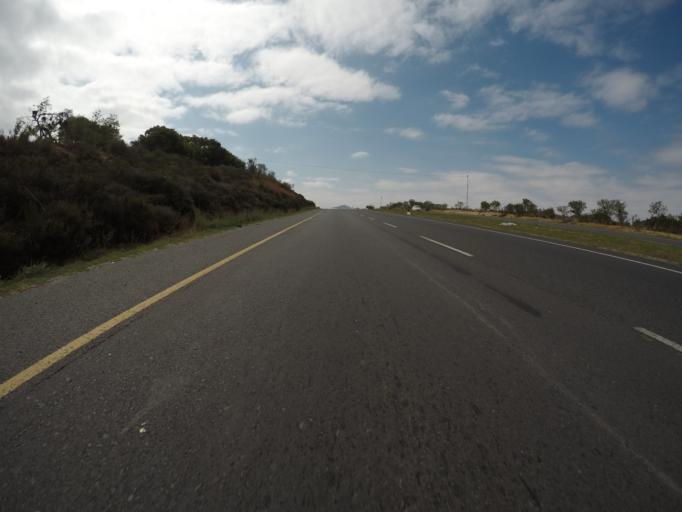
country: ZA
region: Western Cape
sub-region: City of Cape Town
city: Sunset Beach
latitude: -33.7868
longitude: 18.5489
